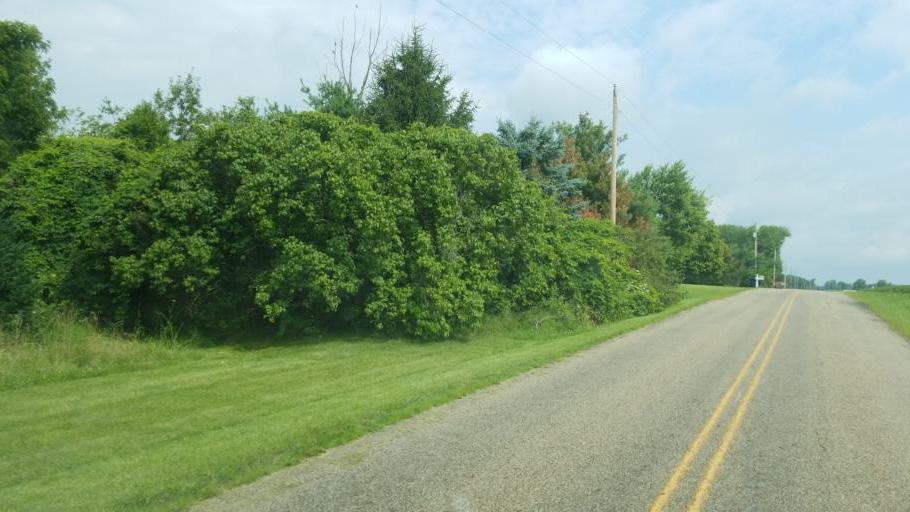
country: US
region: Ohio
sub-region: Knox County
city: Centerburg
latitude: 40.3158
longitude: -82.6257
